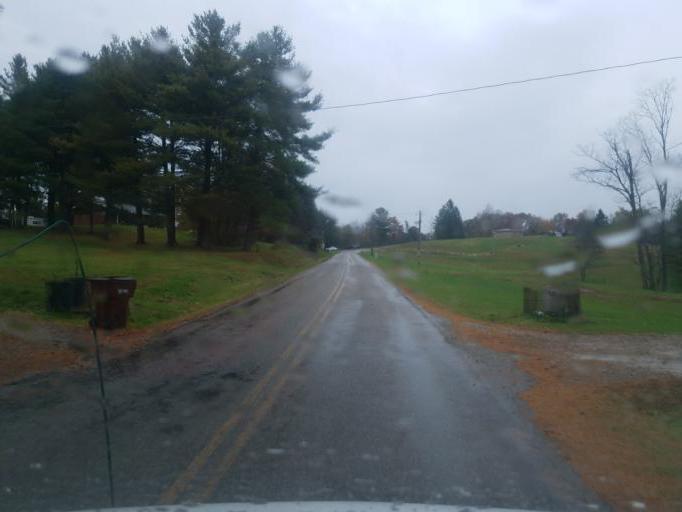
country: US
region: West Virginia
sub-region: Wood County
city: Blennerhassett
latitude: 39.3408
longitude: -81.6276
